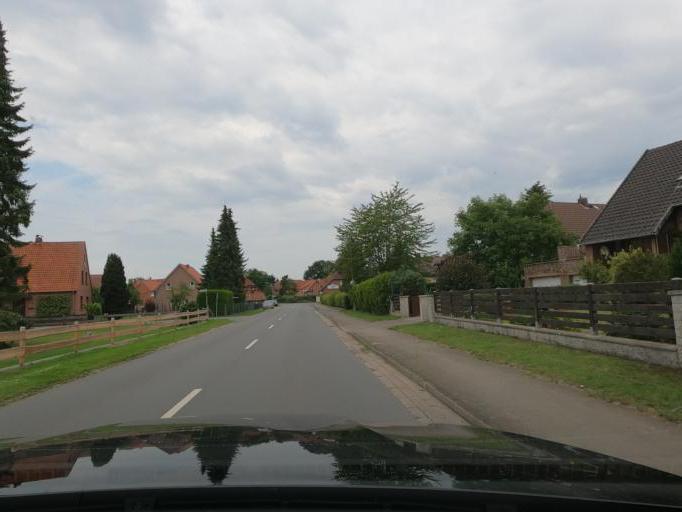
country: DE
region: Lower Saxony
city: Neustadt am Rubenberge
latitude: 52.5502
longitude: 9.5072
